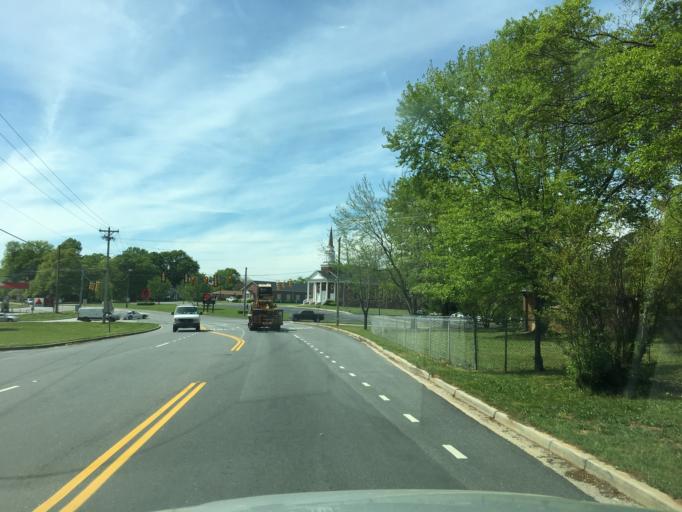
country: US
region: South Carolina
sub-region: Greenville County
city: Wade Hampton
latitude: 34.9038
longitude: -82.3196
